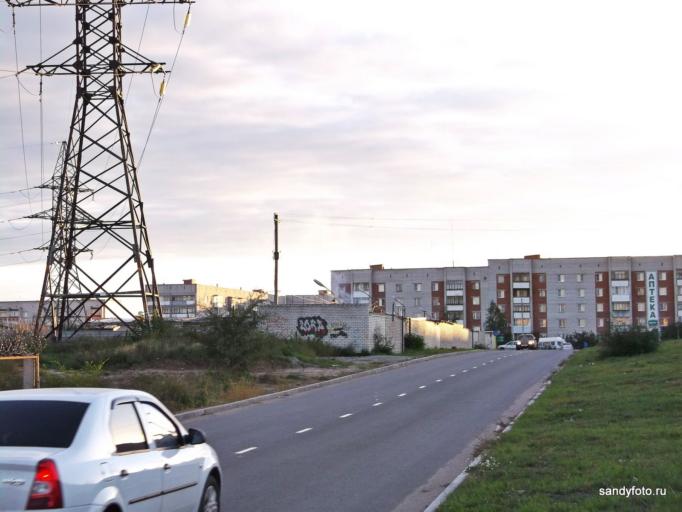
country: RU
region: Chelyabinsk
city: Troitsk
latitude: 54.0752
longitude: 61.5363
